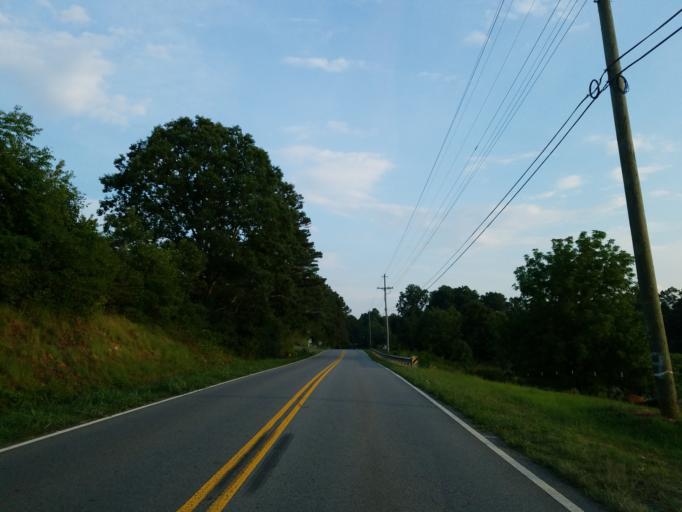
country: US
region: Georgia
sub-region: Gilmer County
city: Ellijay
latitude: 34.6501
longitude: -84.4694
